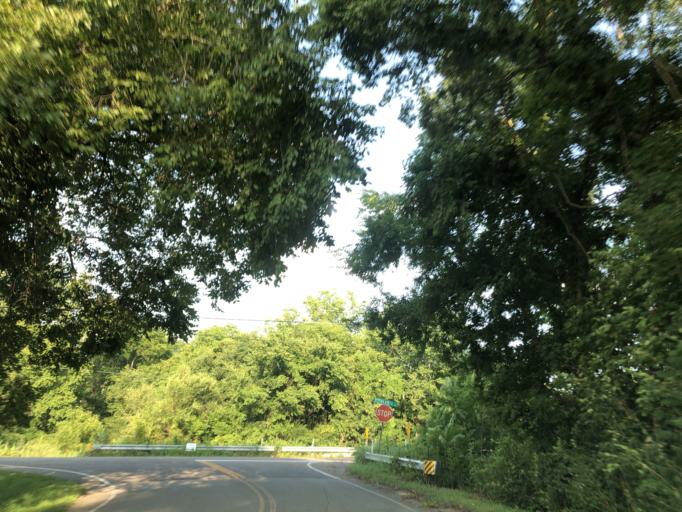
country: US
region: Tennessee
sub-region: Davidson County
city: Nashville
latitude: 36.2475
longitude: -86.8298
